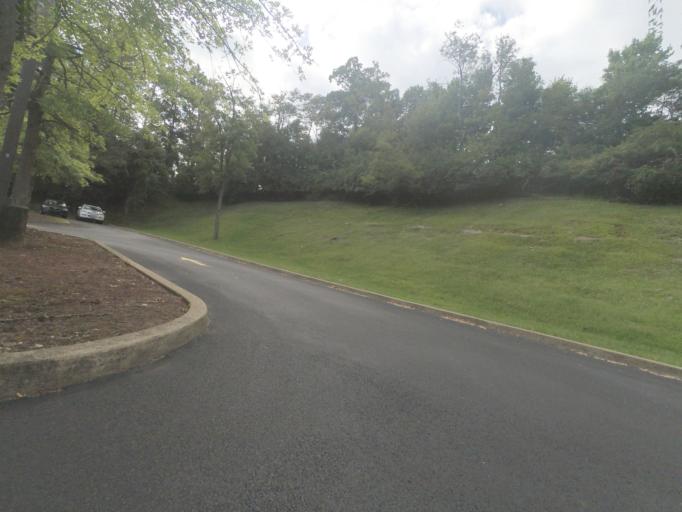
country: US
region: West Virginia
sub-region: Cabell County
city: Huntington
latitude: 38.3933
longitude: -82.4597
